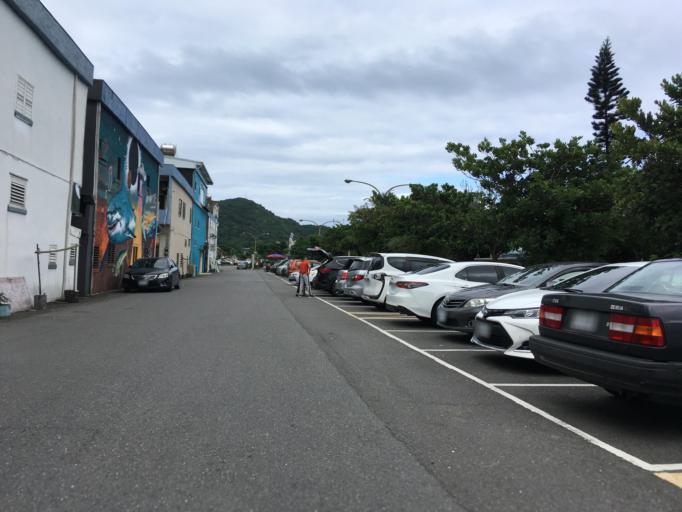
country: TW
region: Taiwan
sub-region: Yilan
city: Yilan
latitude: 24.5768
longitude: 121.8694
